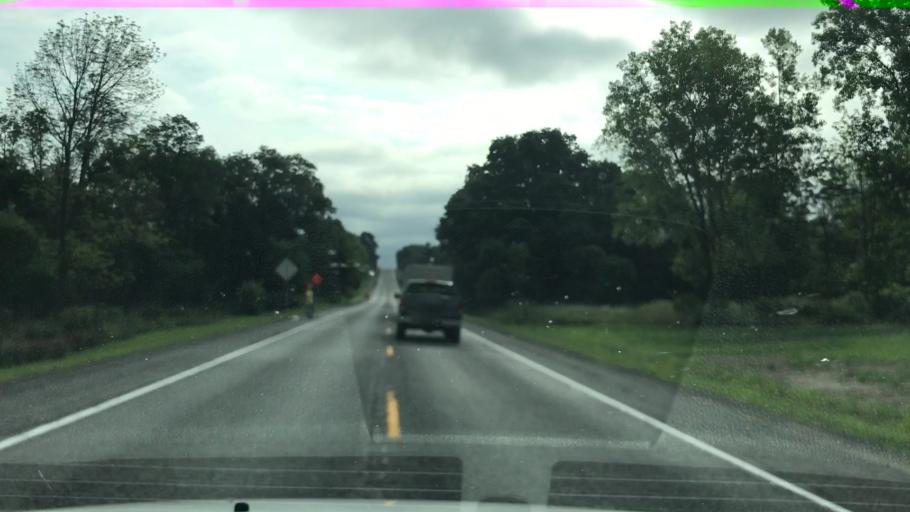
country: US
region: New York
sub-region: Erie County
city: Alden
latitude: 42.8353
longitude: -78.4234
